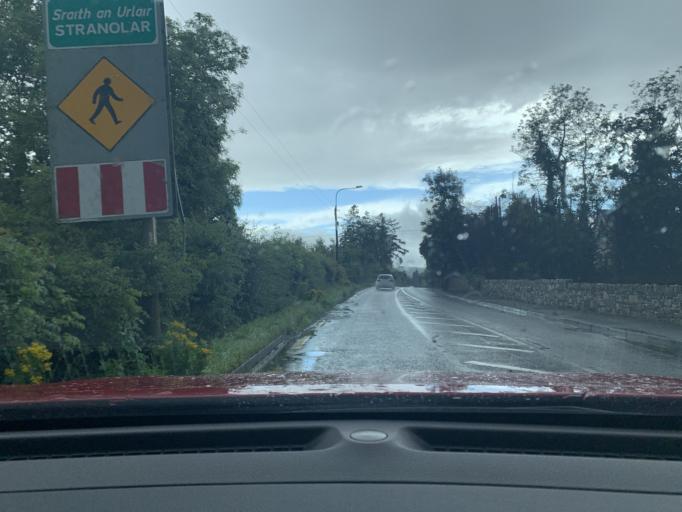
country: IE
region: Ulster
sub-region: County Donegal
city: Ballybofey
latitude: 54.8103
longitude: -7.7641
